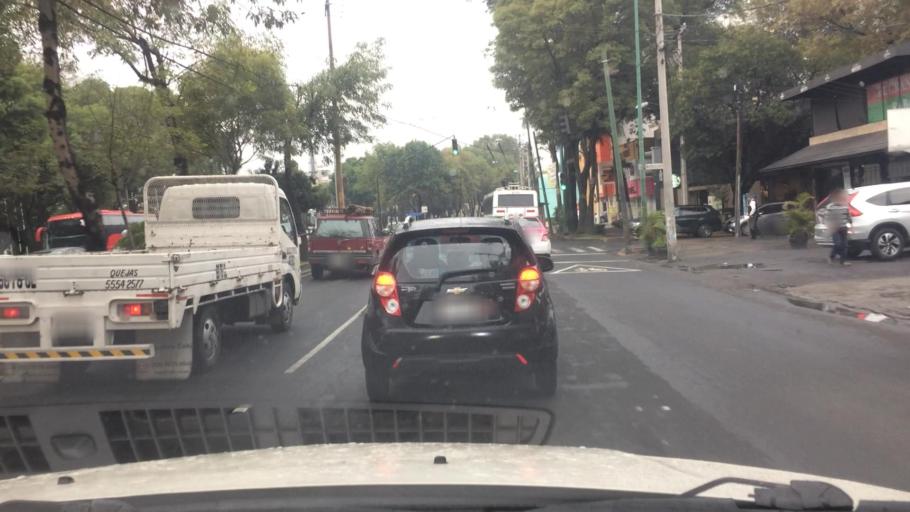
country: MX
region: Mexico City
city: Coyoacan
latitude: 19.3408
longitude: -99.1353
